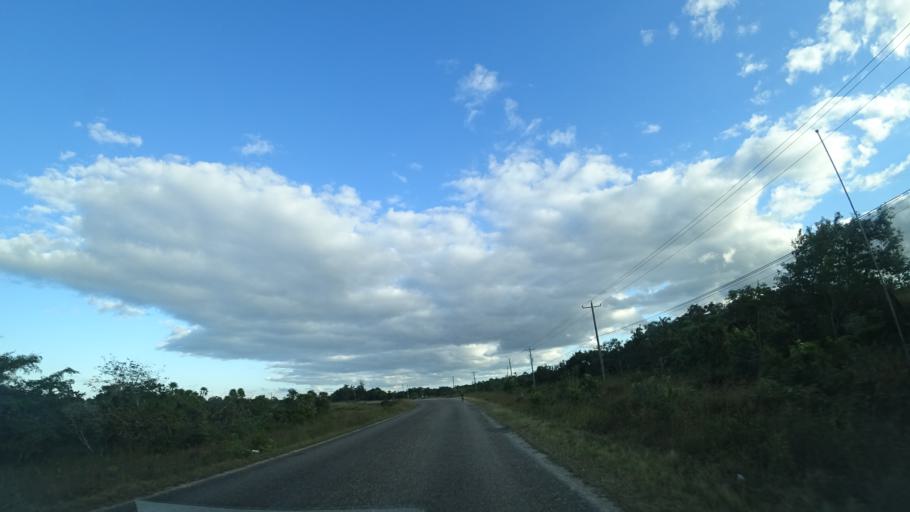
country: BZ
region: Belize
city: Belize City
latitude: 17.5804
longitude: -88.3725
